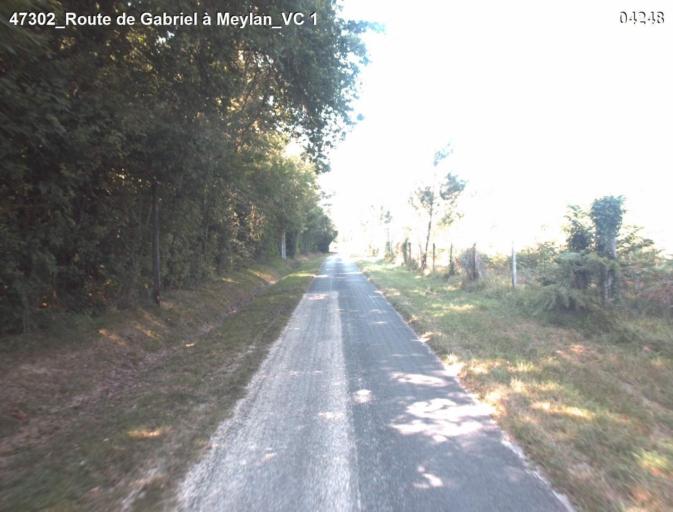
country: FR
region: Aquitaine
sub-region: Departement des Landes
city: Gabarret
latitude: 44.0788
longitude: 0.1153
